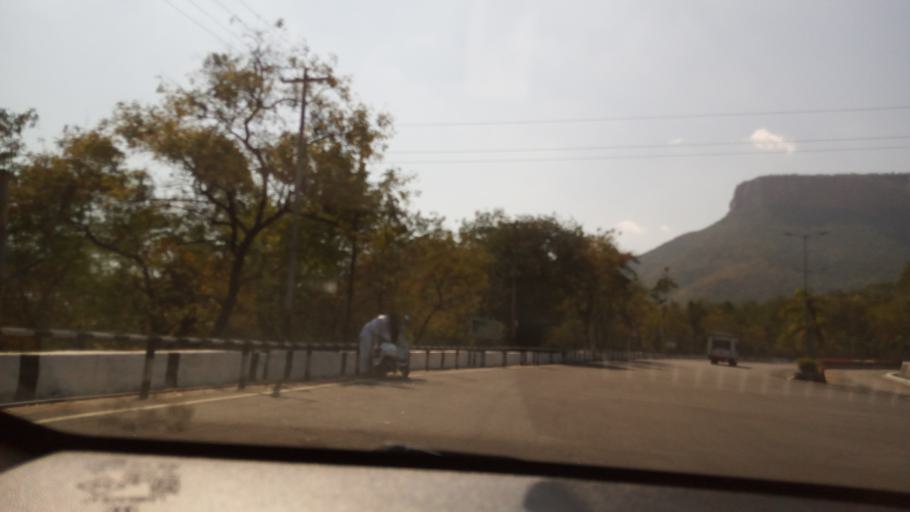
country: IN
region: Andhra Pradesh
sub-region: Chittoor
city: Akkarampalle
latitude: 13.6467
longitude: 79.4008
